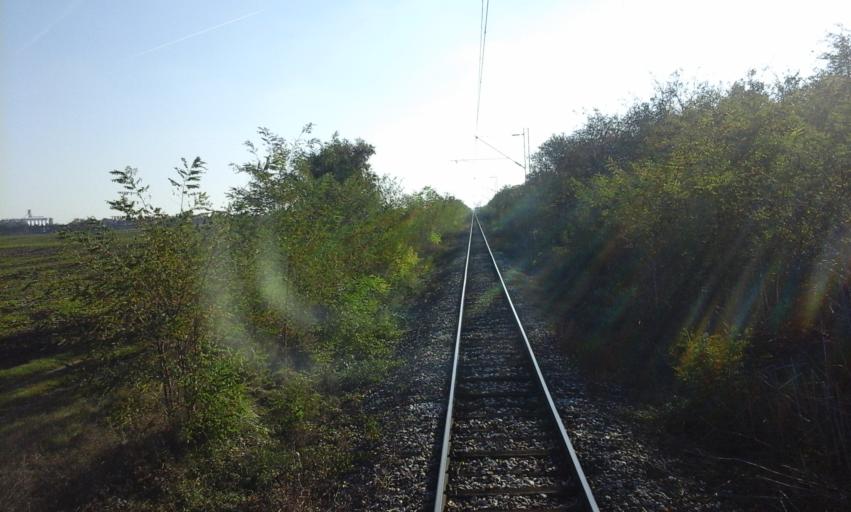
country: RS
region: Autonomna Pokrajina Vojvodina
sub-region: Severnobacki Okrug
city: Backa Topola
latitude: 45.7866
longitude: 19.6476
